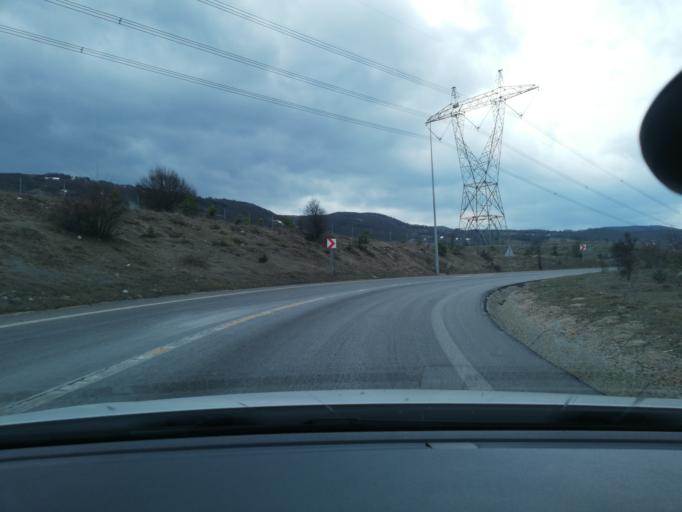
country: TR
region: Bolu
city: Yenicaga
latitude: 40.7627
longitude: 32.0099
